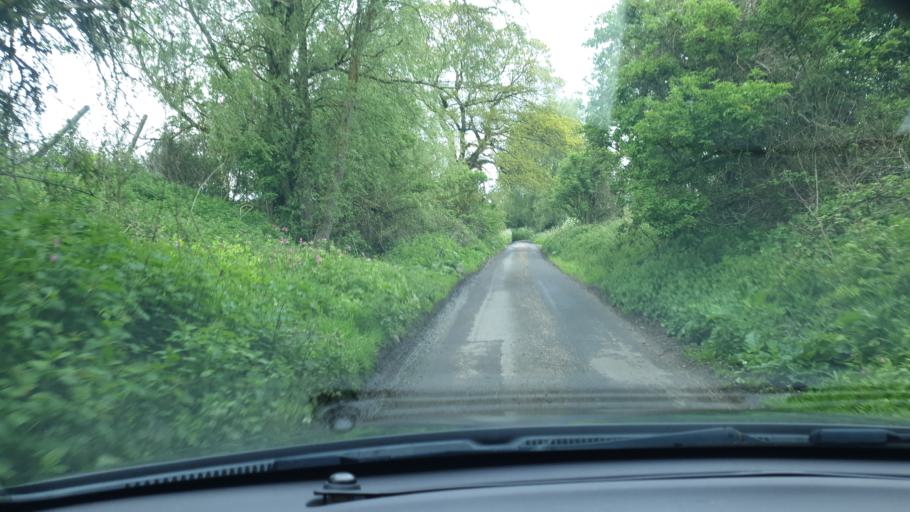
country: GB
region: England
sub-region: Essex
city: Dovercourt
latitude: 51.9095
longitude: 1.1987
